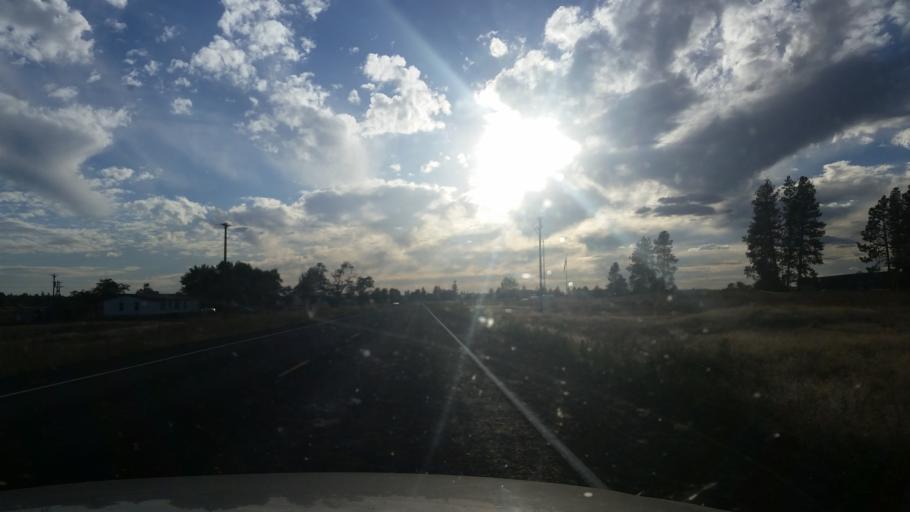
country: US
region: Washington
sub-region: Spokane County
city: Cheney
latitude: 47.4661
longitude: -117.6418
